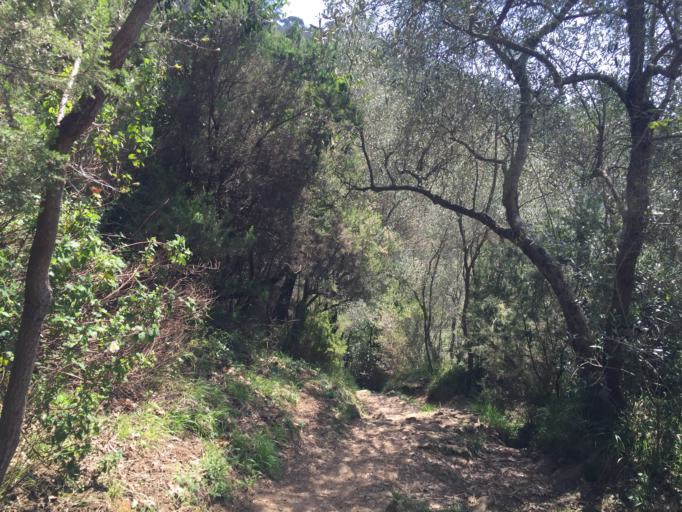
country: IT
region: Liguria
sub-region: Provincia di Genova
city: Portofino
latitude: 44.3200
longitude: 9.1785
